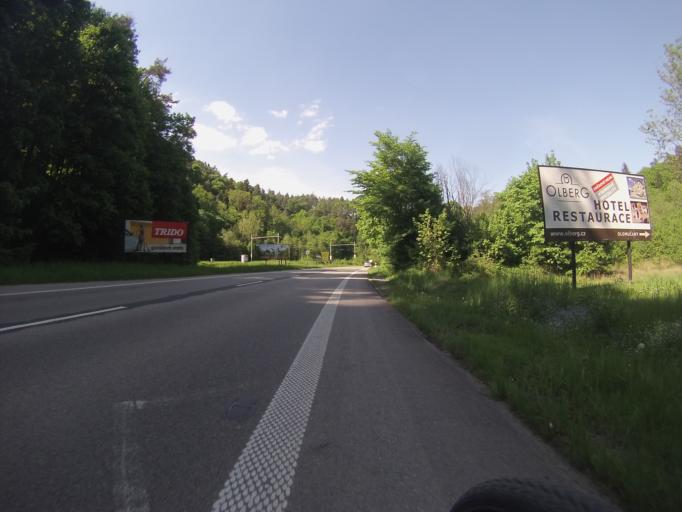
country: CZ
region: South Moravian
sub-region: Okres Blansko
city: Blansko
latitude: 49.3378
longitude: 16.6487
